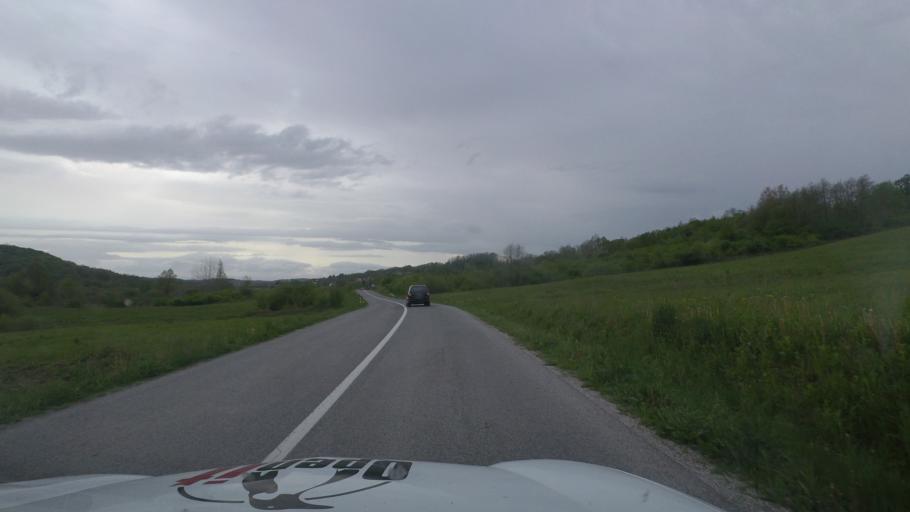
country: HR
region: Karlovacka
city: Vojnic
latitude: 45.3780
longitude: 15.6428
